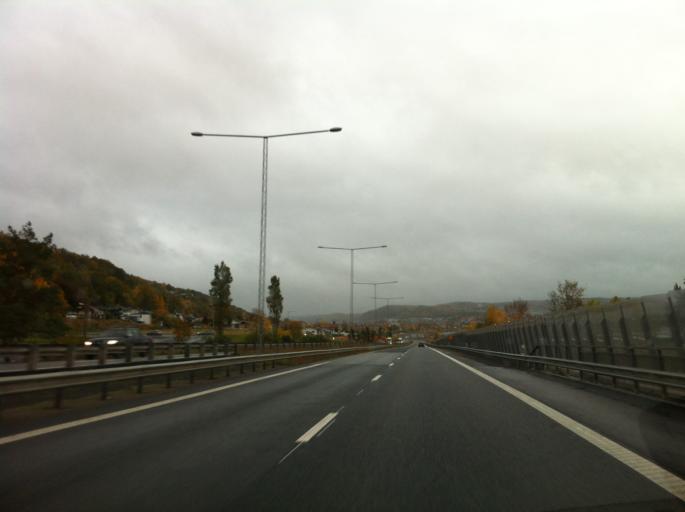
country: SE
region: Joenkoeping
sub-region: Jonkopings Kommun
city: Huskvarna
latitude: 57.8169
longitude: 14.2716
